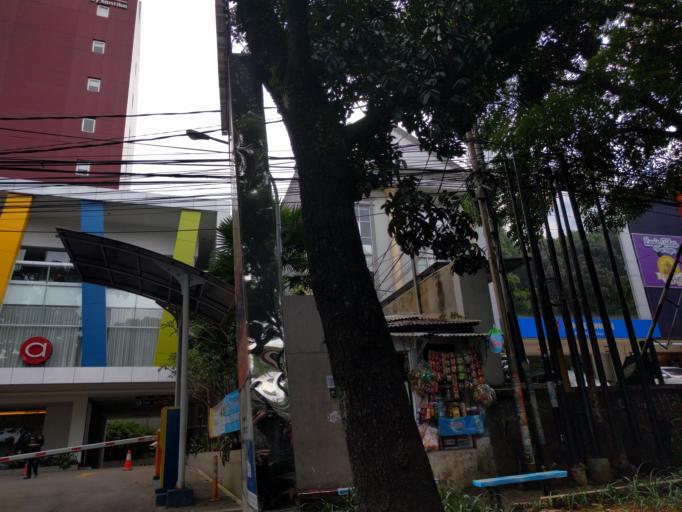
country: ID
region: West Java
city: Bogor
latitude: -6.6081
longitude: 106.8101
